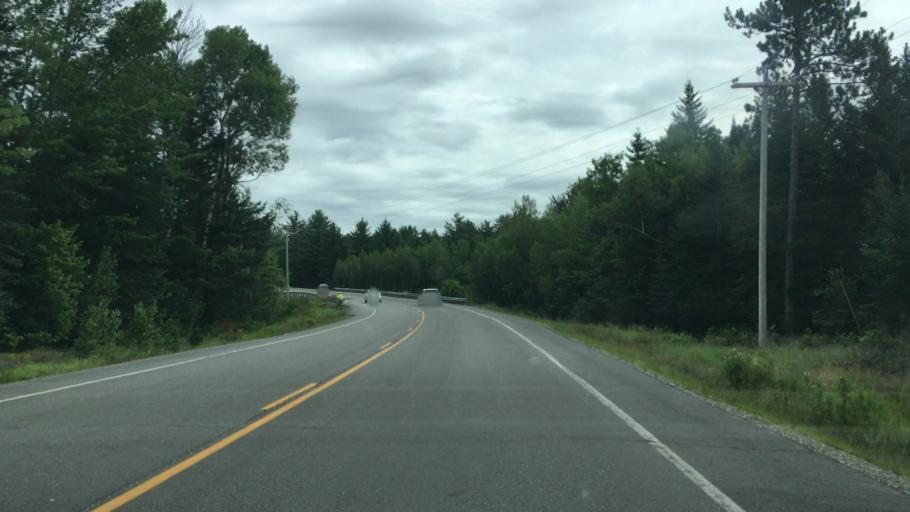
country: US
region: Maine
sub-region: Washington County
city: Machias
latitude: 44.9994
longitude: -67.5873
